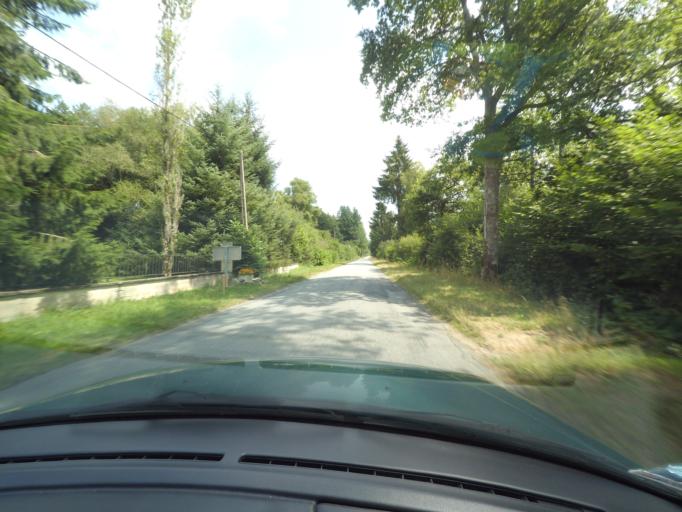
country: FR
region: Limousin
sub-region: Departement de la Correze
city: Bugeat
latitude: 45.7512
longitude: 1.9397
